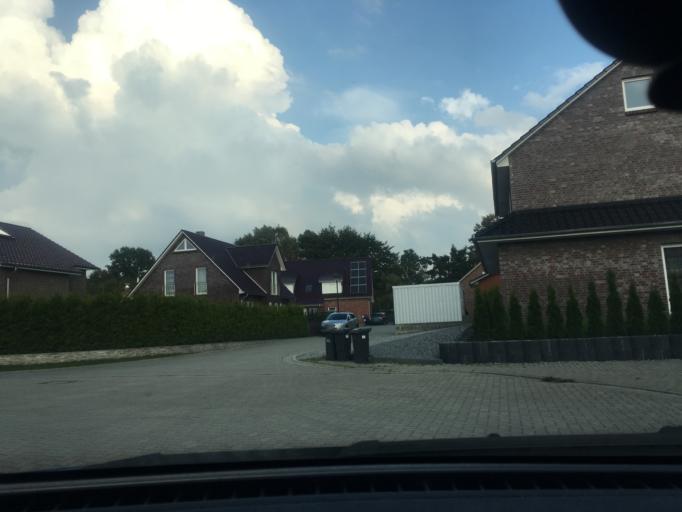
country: DE
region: Lower Saxony
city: Barendorf
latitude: 53.2266
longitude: 10.5174
